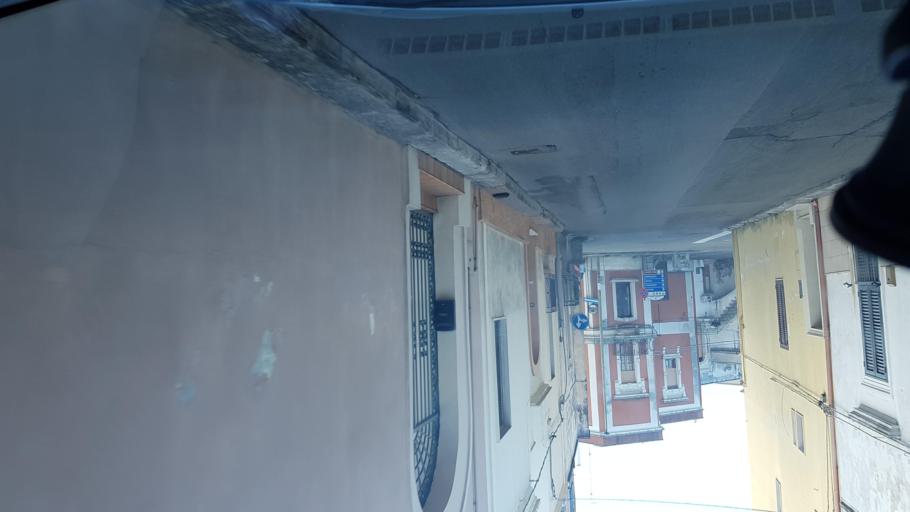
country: IT
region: Apulia
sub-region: Provincia di Lecce
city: Veglie
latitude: 40.3358
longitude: 17.9715
